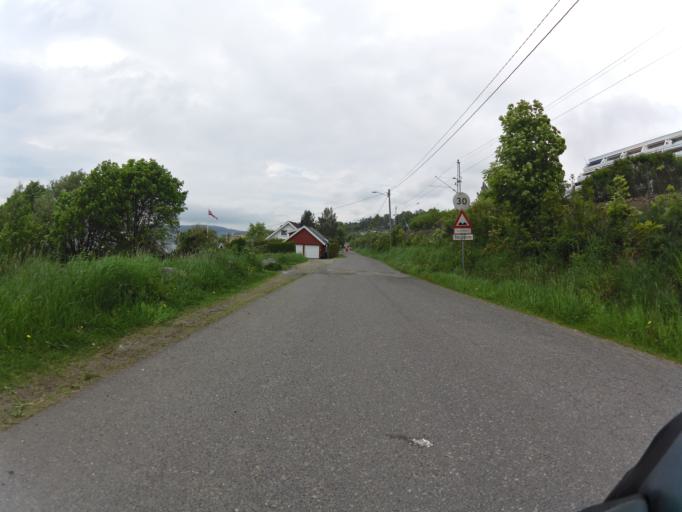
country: NO
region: Ostfold
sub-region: Moss
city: Moss
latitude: 59.4142
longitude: 10.6568
